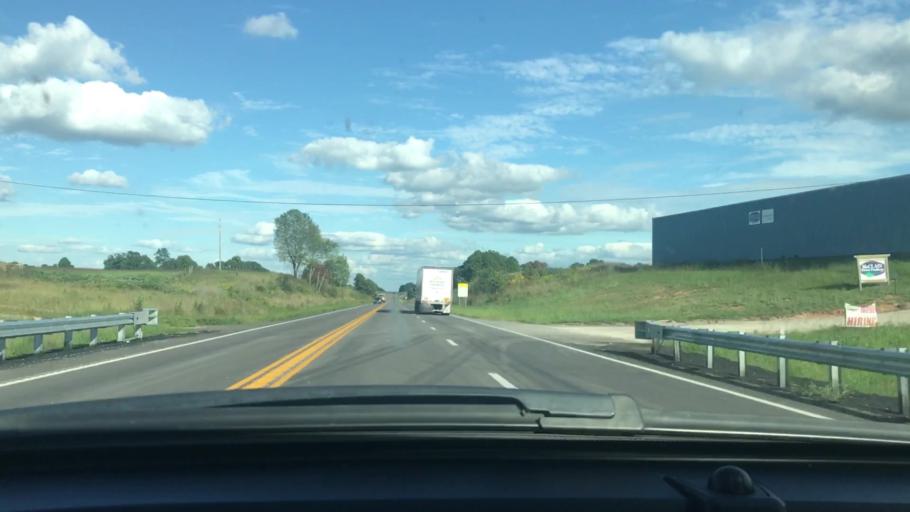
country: US
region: Missouri
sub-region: Oregon County
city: Thayer
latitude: 36.5879
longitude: -91.6339
